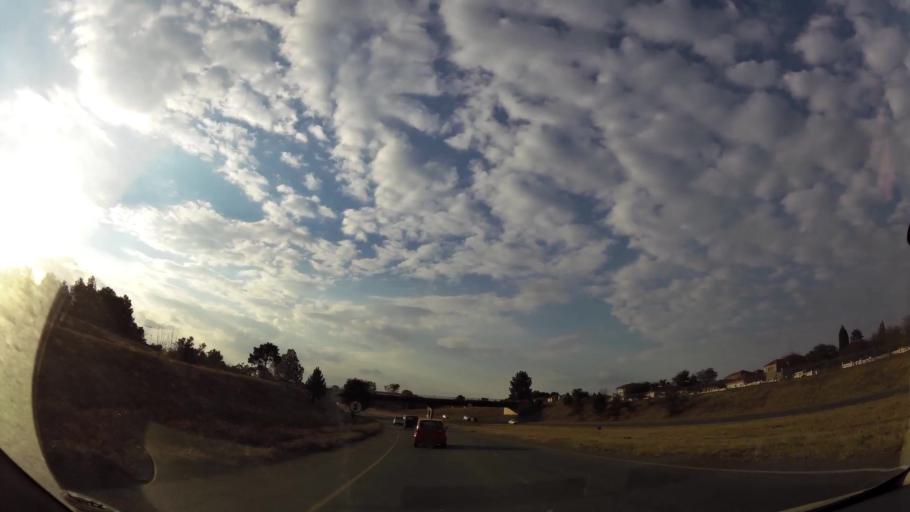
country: ZA
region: Gauteng
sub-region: Sedibeng District Municipality
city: Vanderbijlpark
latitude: -26.7510
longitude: 27.8260
